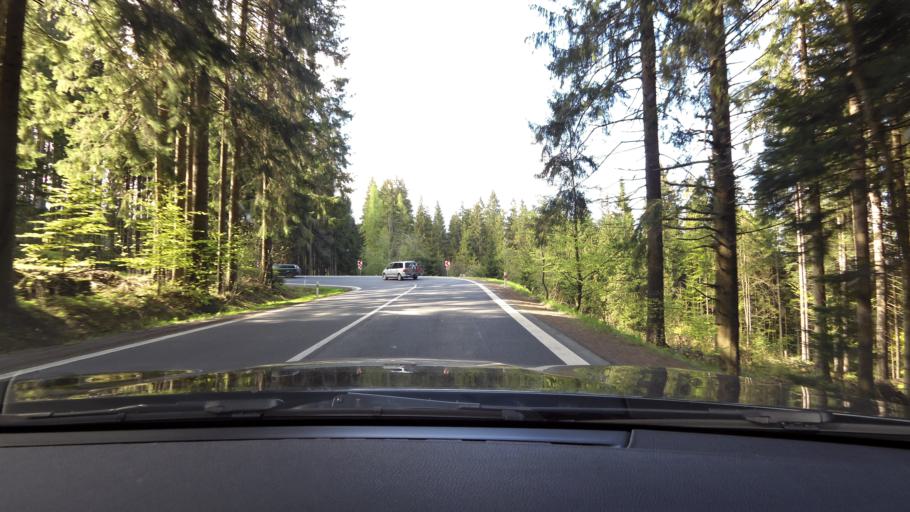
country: CZ
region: Plzensky
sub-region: Okres Klatovy
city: Zelezna Ruda
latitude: 49.1999
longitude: 13.3023
